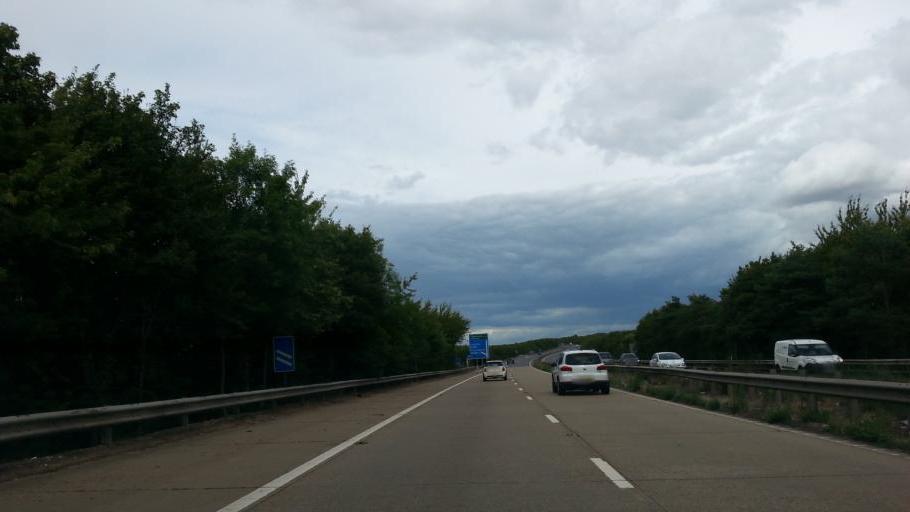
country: GB
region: England
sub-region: Cambridgeshire
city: Duxford
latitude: 52.0690
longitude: 0.1870
